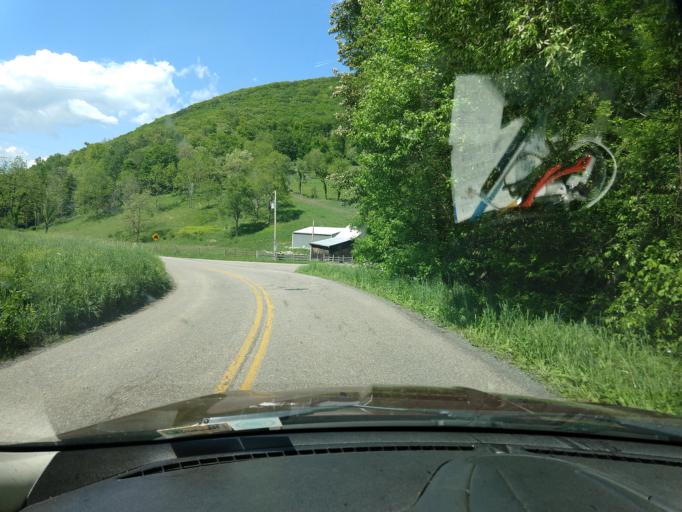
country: US
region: Virginia
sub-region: City of Covington
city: Fairlawn
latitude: 37.7429
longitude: -79.9123
